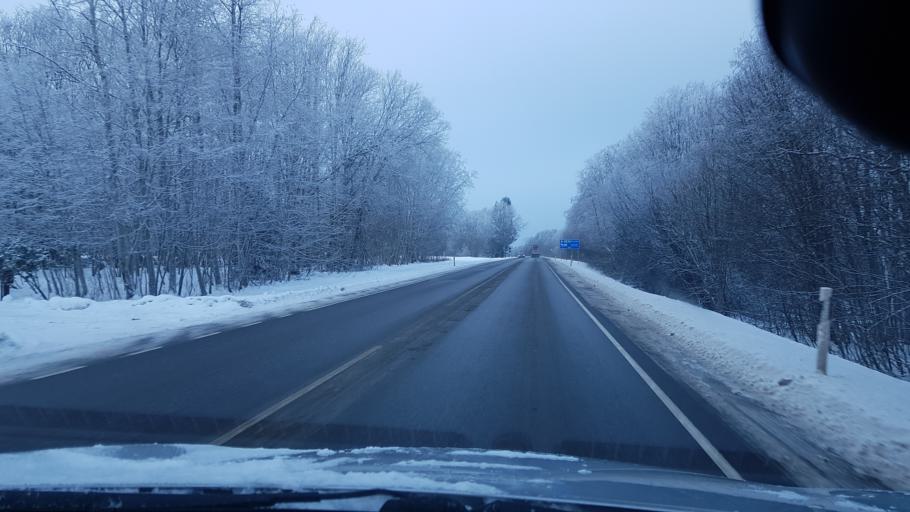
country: EE
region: Harju
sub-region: Paldiski linn
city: Paldiski
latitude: 59.3404
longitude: 24.2011
